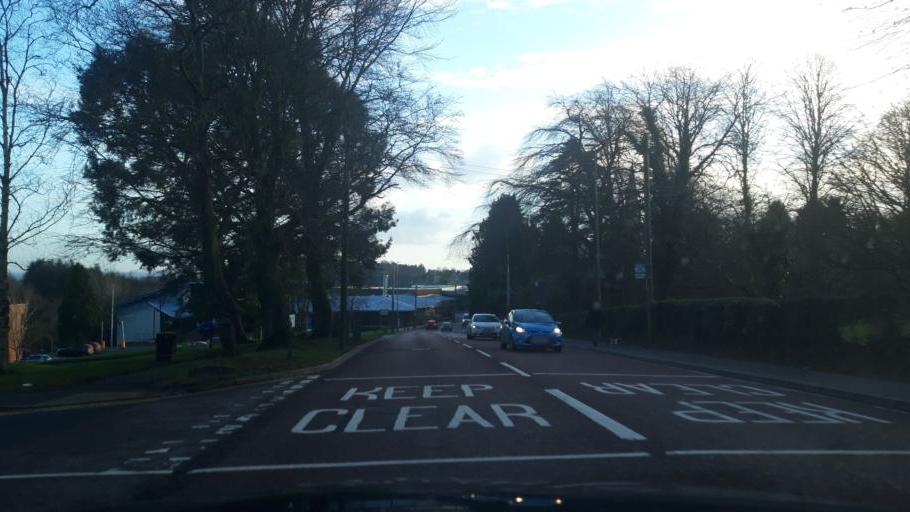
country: GB
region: Northern Ireland
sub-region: Dungannon District
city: Dungannon
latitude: 54.5083
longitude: -6.7642
